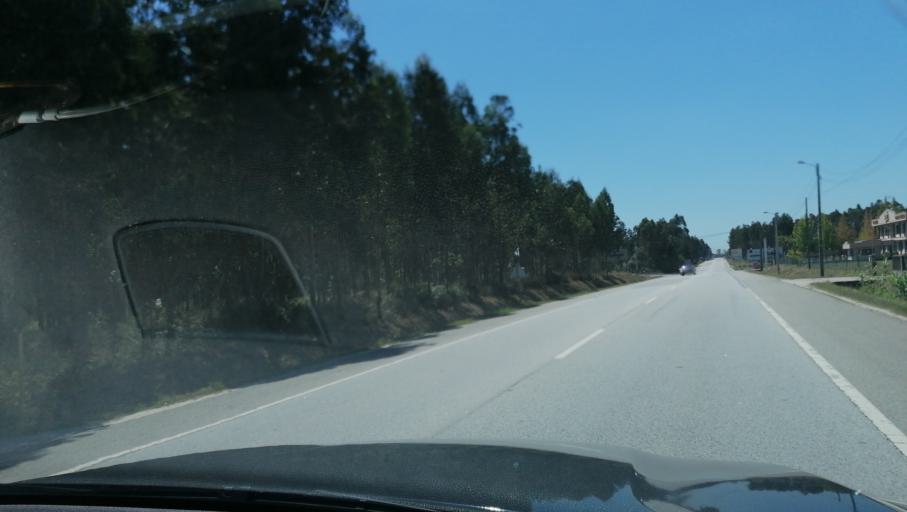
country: PT
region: Aveiro
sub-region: Anadia
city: Sangalhos
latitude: 40.4981
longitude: -8.4431
